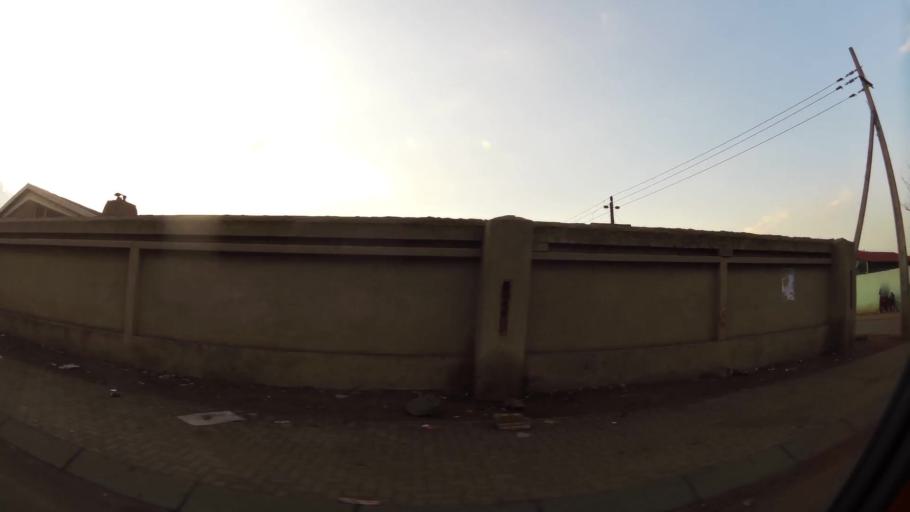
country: ZA
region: Gauteng
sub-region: City of Johannesburg Metropolitan Municipality
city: Orange Farm
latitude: -26.5361
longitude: 27.8388
